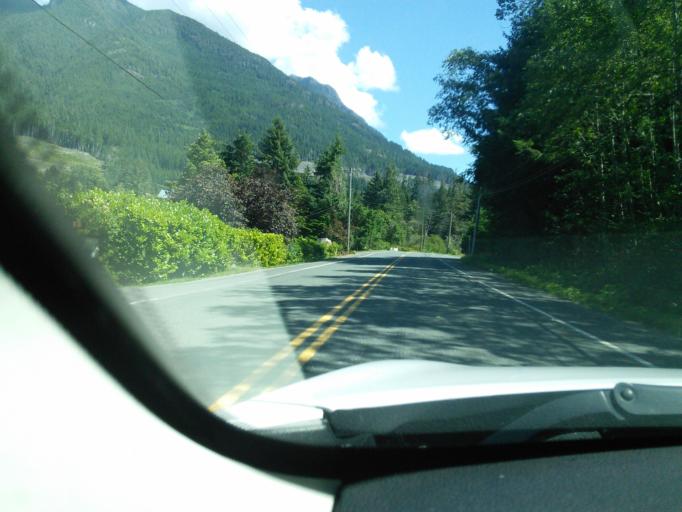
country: CA
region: British Columbia
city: Campbell River
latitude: 50.3544
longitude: -125.9102
